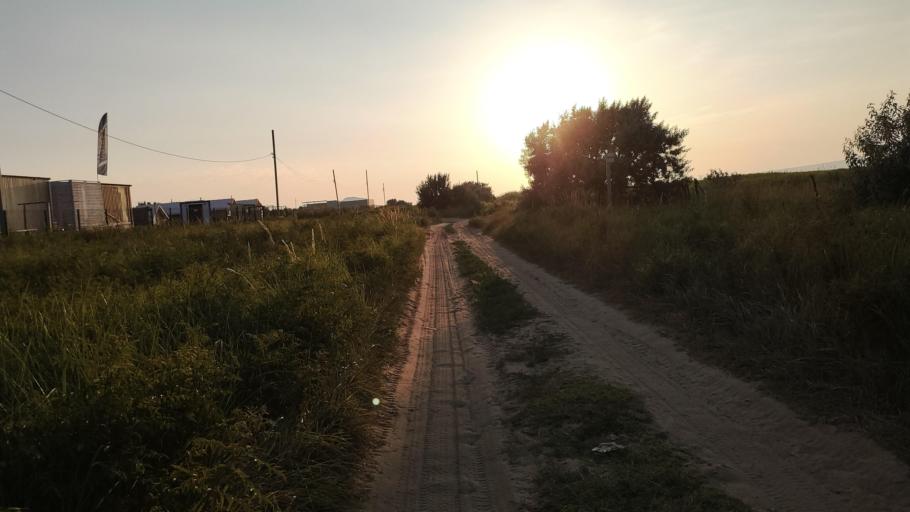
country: RU
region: Krasnodarskiy
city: Blagovetschenskaya
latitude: 45.0672
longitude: 37.0375
